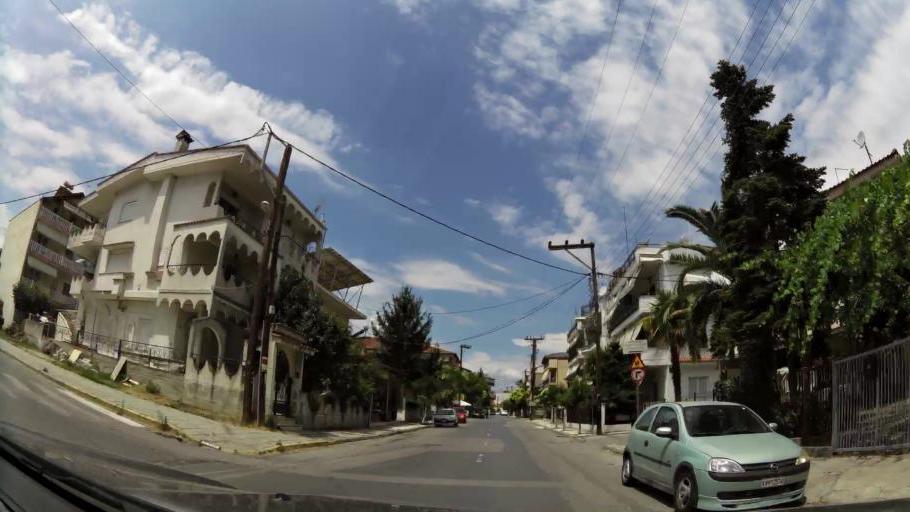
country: GR
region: Central Macedonia
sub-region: Nomos Pierias
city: Katerini
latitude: 40.2674
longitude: 22.5182
